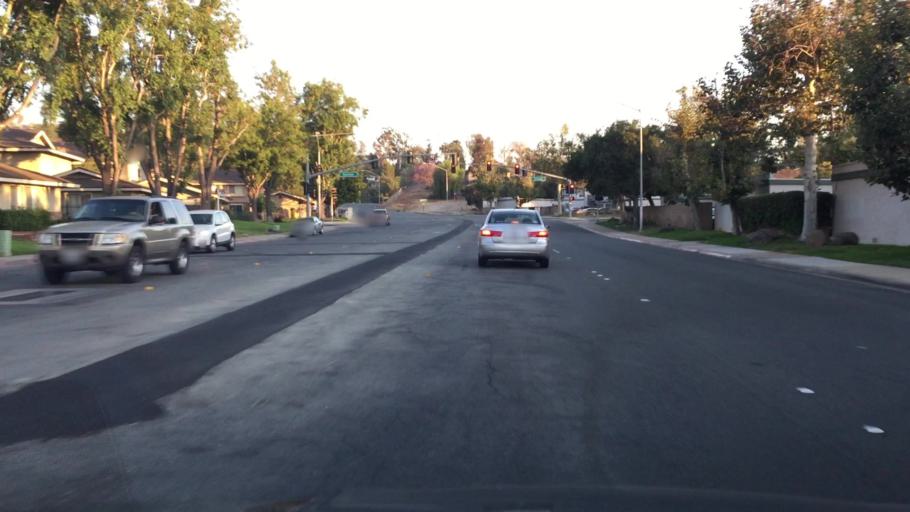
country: US
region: California
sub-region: San Diego County
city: Bostonia
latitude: 32.7833
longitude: -116.9280
